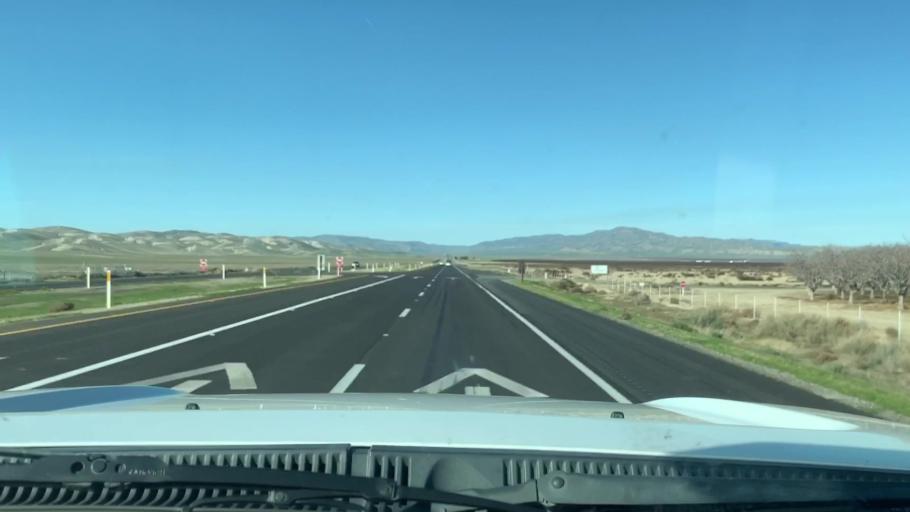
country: US
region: California
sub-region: Kern County
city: Lost Hills
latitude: 35.6192
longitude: -119.9740
